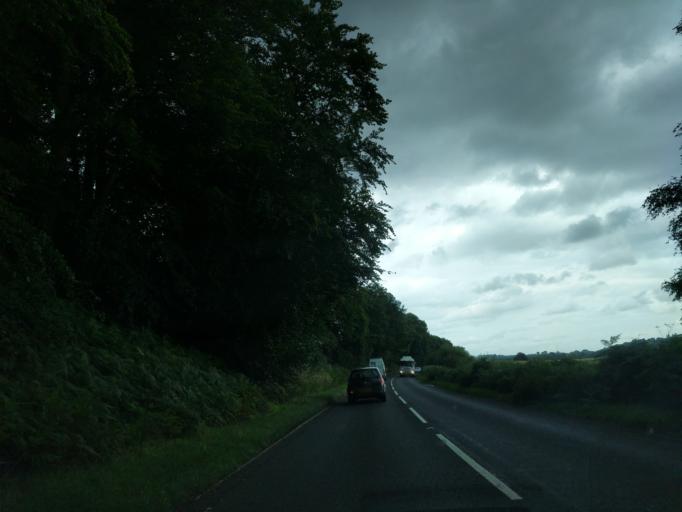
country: GB
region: England
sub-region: Staffordshire
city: Colwich
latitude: 52.7804
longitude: -1.9758
